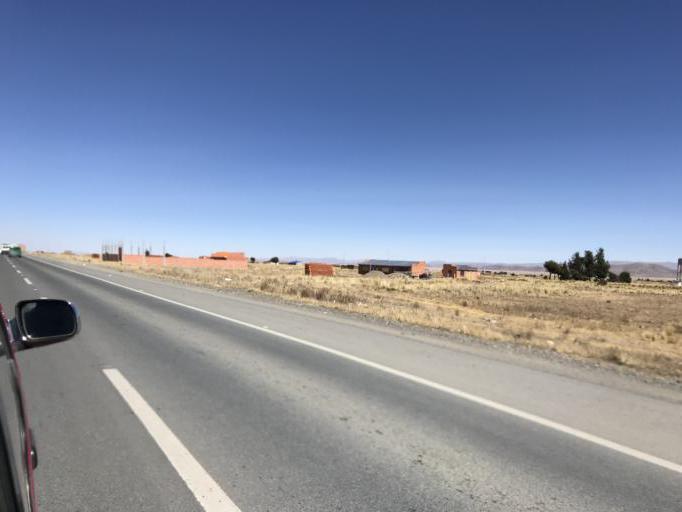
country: BO
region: La Paz
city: Batallas
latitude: -16.3494
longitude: -68.4037
